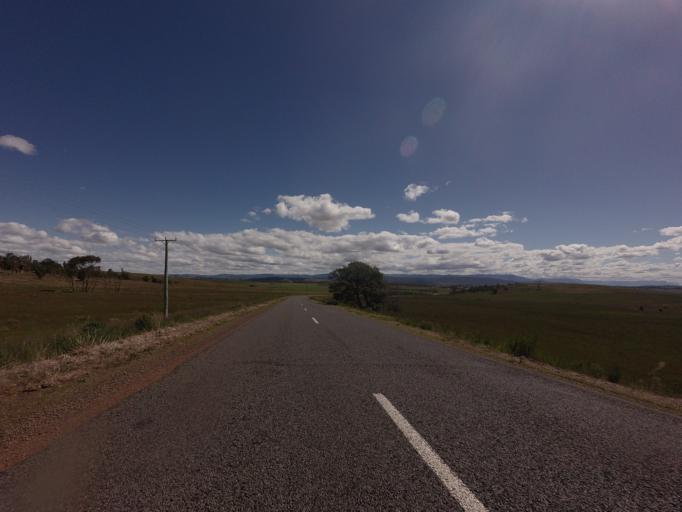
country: AU
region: Tasmania
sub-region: Northern Midlands
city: Evandale
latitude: -41.9385
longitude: 147.5696
